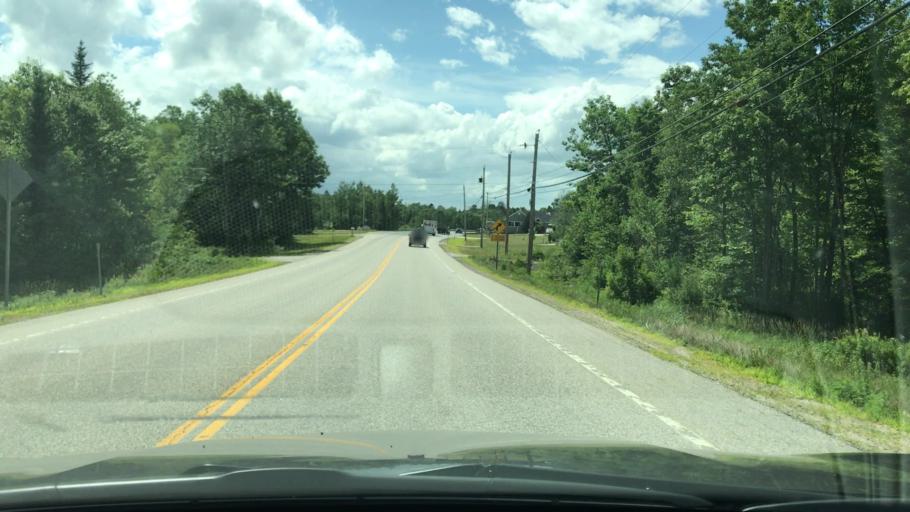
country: US
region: New Hampshire
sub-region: Coos County
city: Jefferson
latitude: 44.3590
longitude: -71.3631
